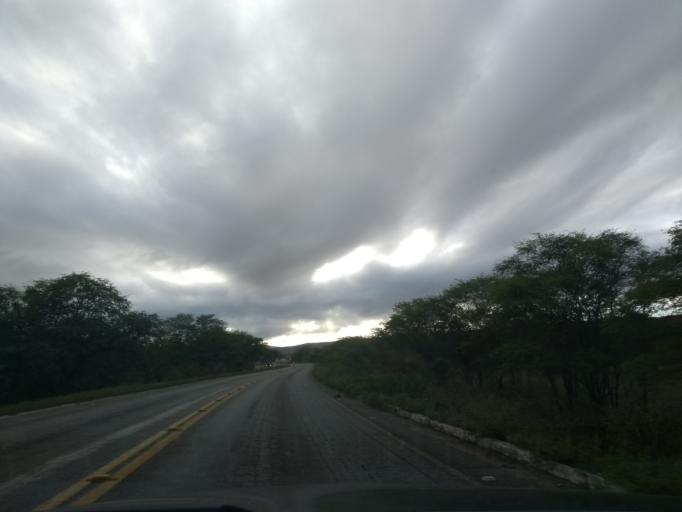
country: BR
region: Bahia
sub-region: Ituacu
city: Ituacu
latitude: -13.7667
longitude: -41.0410
